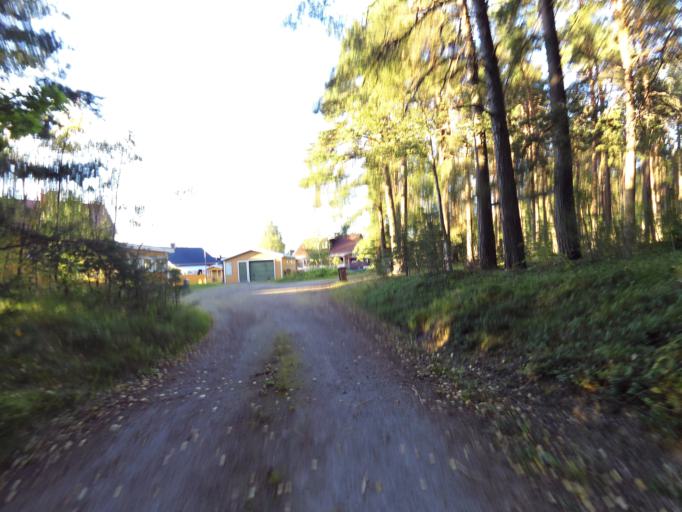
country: SE
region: Gaevleborg
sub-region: Gavle Kommun
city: Gavle
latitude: 60.7115
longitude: 17.1632
